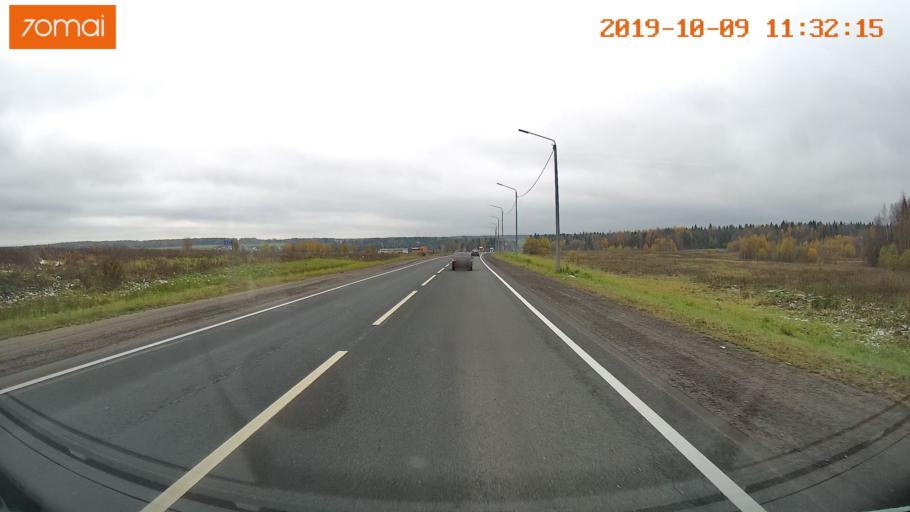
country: RU
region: Vologda
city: Gryazovets
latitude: 59.0376
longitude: 40.1071
